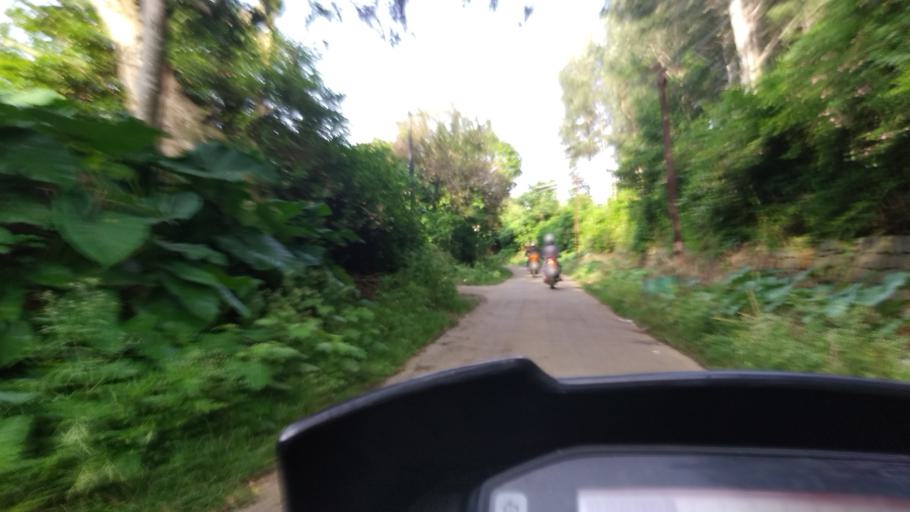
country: IN
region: Tamil Nadu
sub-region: Salem
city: Salem
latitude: 11.7702
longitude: 78.2115
